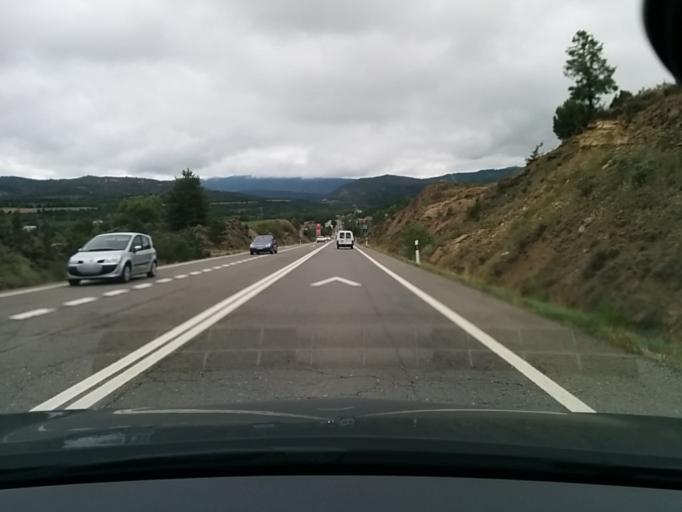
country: ES
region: Aragon
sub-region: Provincia de Huesca
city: Sabinanigo
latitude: 42.4320
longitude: -0.3976
